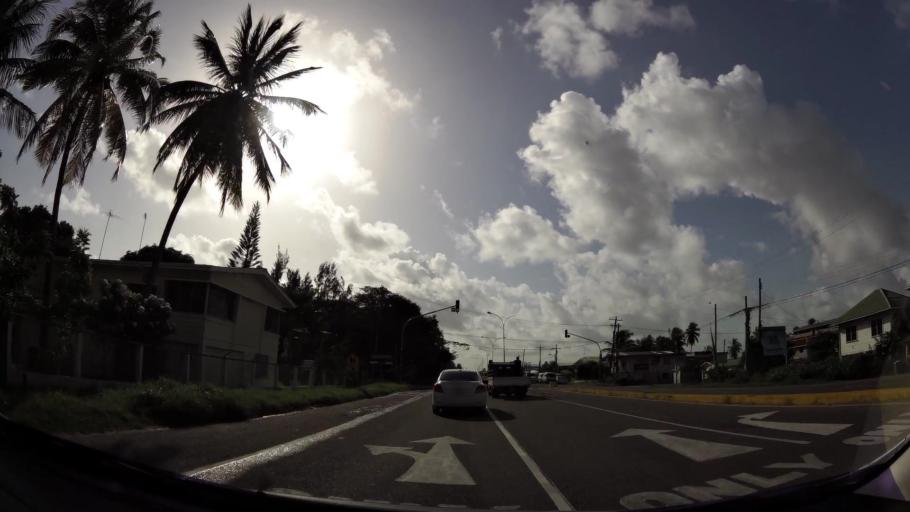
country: GY
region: Demerara-Mahaica
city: Georgetown
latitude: 6.8214
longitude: -58.0975
